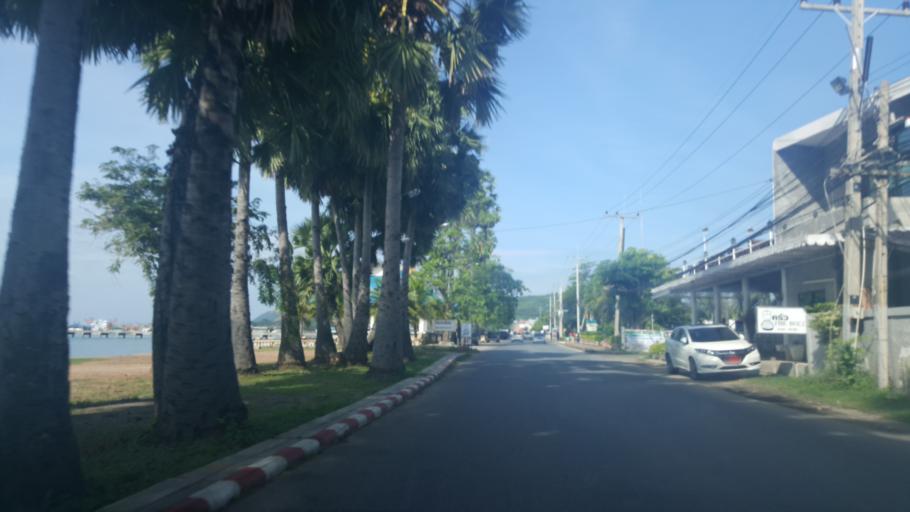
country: TH
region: Chon Buri
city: Sattahip
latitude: 12.6623
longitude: 100.9065
